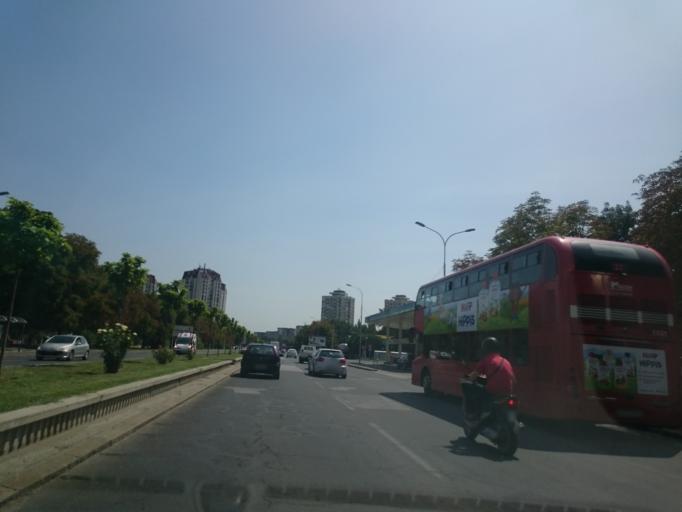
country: MK
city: Krushopek
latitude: 42.0067
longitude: 21.3758
